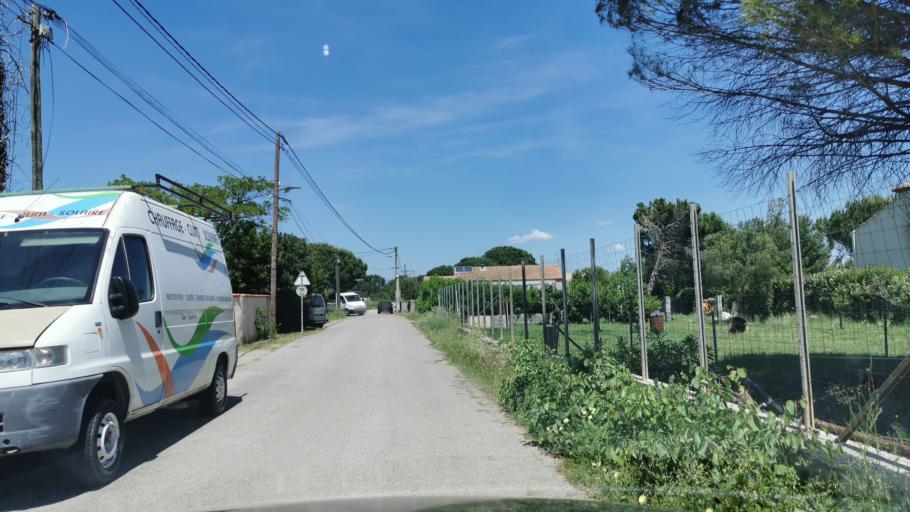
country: FR
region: Languedoc-Roussillon
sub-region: Departement de l'Aude
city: Coursan
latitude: 43.2687
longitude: 3.0229
